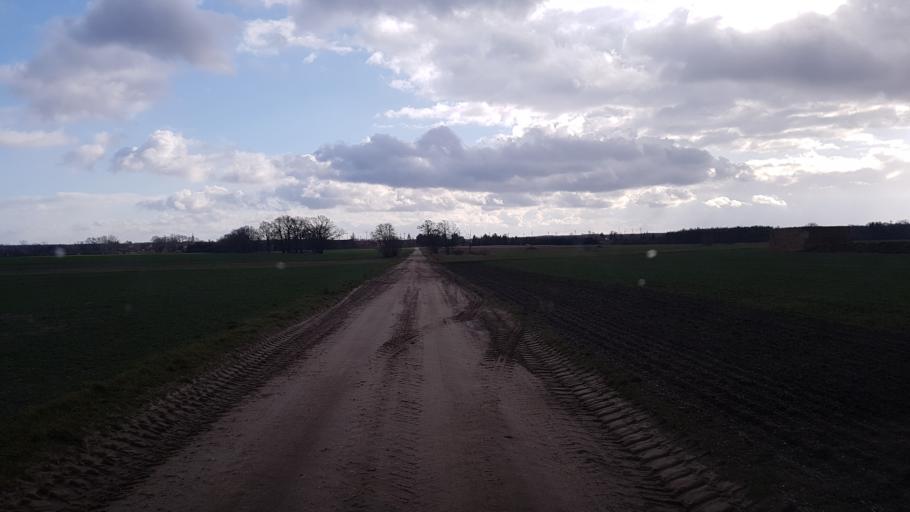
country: DE
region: Brandenburg
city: Sallgast
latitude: 51.6179
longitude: 13.8559
